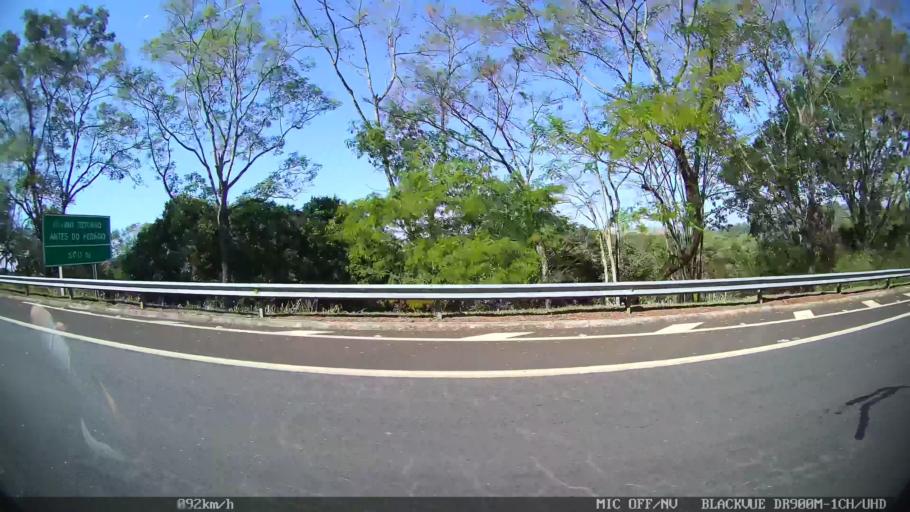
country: BR
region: Sao Paulo
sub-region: Batatais
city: Batatais
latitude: -20.7259
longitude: -47.5168
